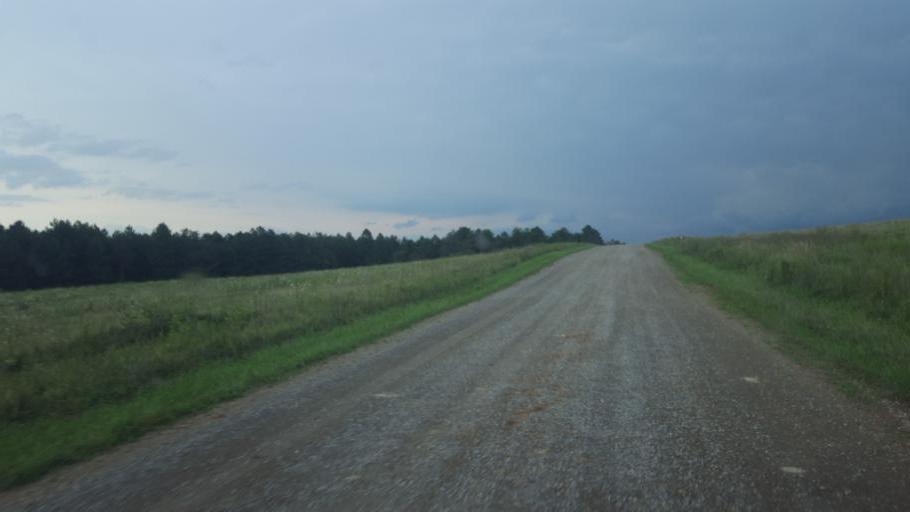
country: US
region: Pennsylvania
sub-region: Clarion County
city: Knox
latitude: 41.1462
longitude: -79.5011
